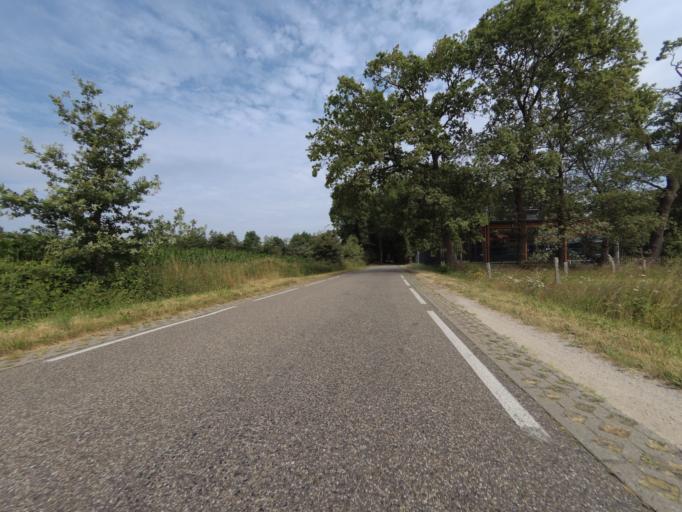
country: NL
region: Overijssel
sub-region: Gemeente Hengelo
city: Hengelo
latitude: 52.2153
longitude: 6.7767
